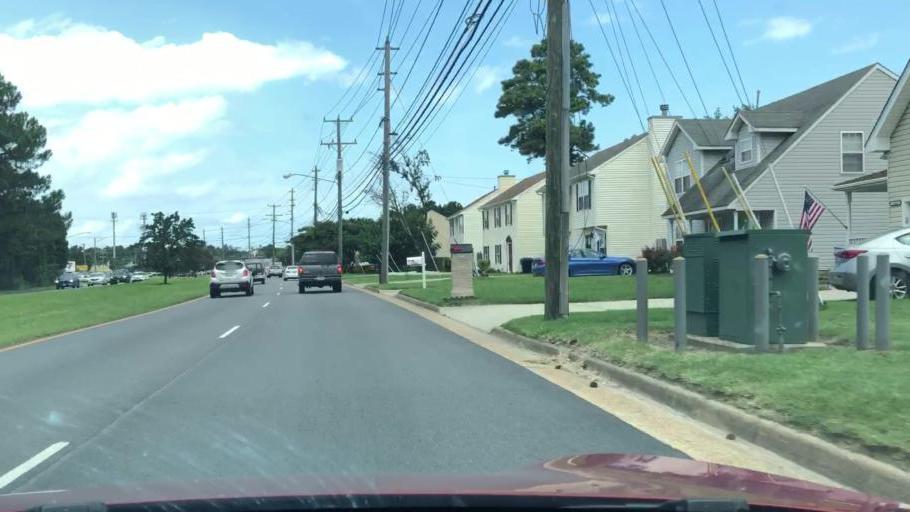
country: US
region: Virginia
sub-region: City of Norfolk
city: Norfolk
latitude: 36.8912
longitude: -76.1389
